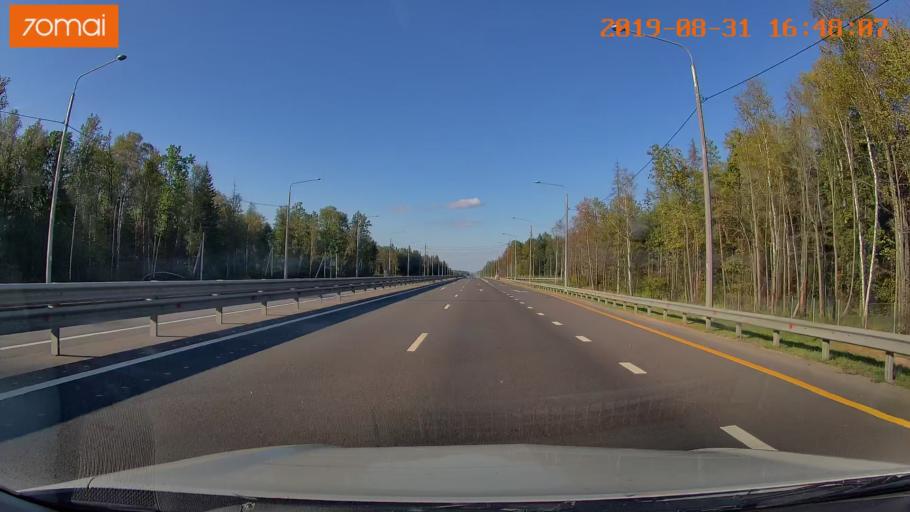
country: RU
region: Kaluga
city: Pyatovskiy
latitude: 54.6665
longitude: 36.1443
